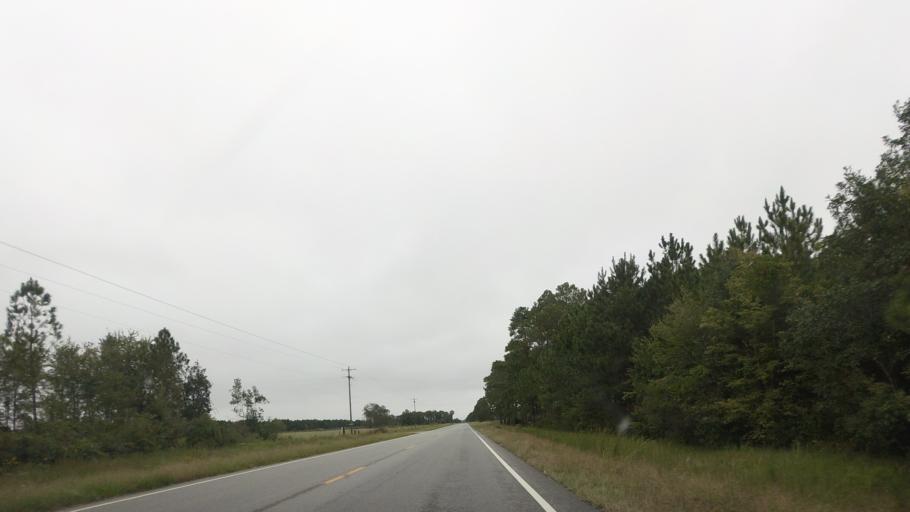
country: US
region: Georgia
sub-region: Berrien County
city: Nashville
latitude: 31.3183
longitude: -83.2312
